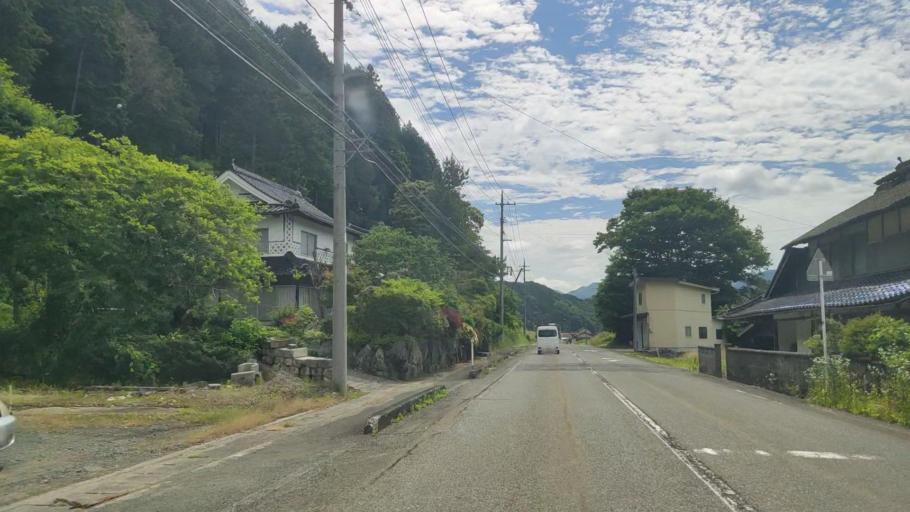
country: JP
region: Okayama
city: Niimi
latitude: 35.1641
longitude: 133.5961
